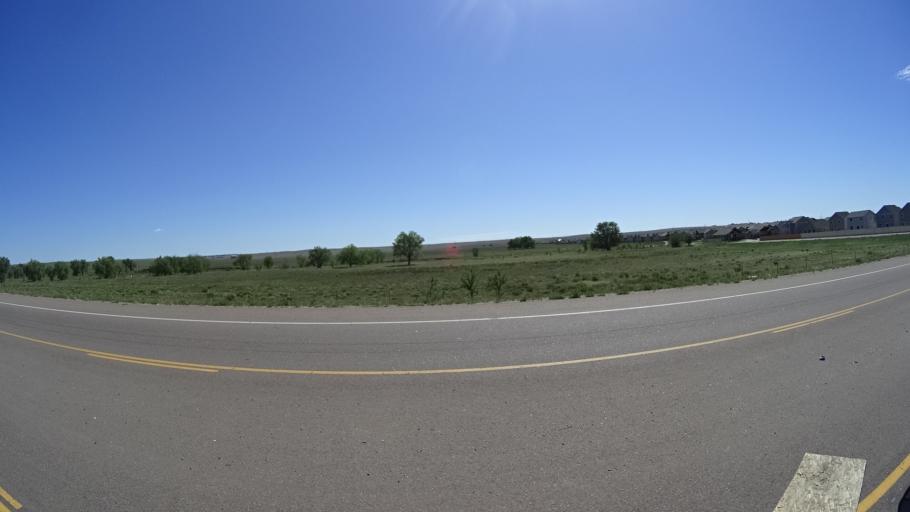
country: US
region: Colorado
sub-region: El Paso County
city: Security-Widefield
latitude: 38.7457
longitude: -104.6485
